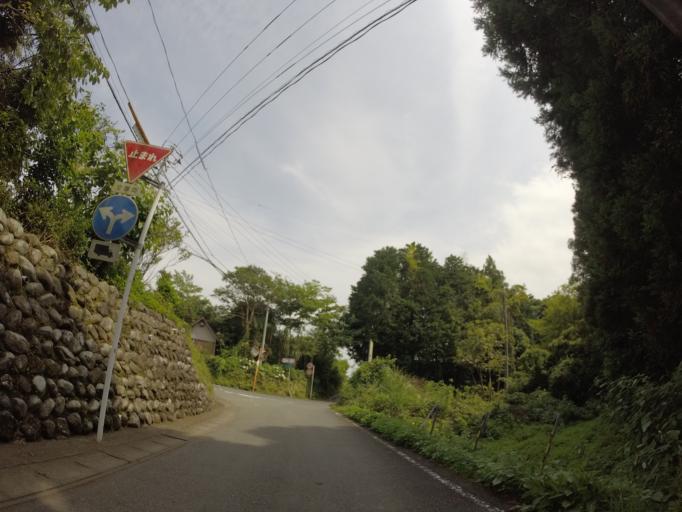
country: JP
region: Shizuoka
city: Fujinomiya
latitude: 35.2772
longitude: 138.5717
